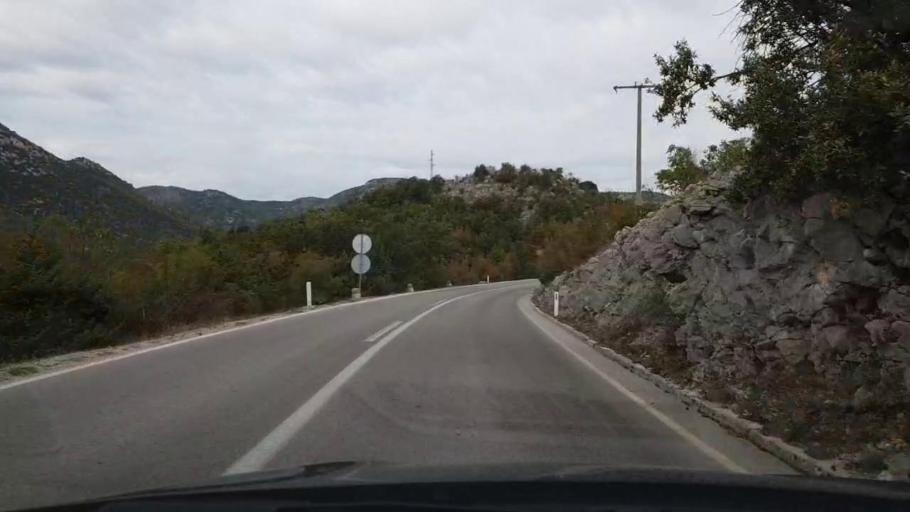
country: HR
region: Dubrovacko-Neretvanska
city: Cibaca
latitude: 42.6611
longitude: 18.2106
